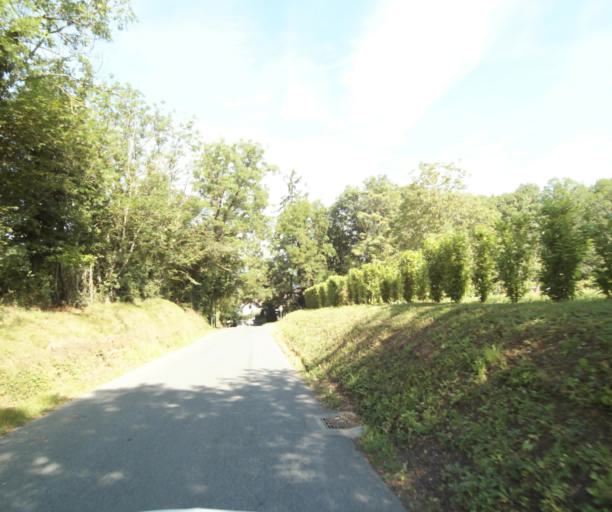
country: FR
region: Rhone-Alpes
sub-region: Departement de la Haute-Savoie
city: Anthy-sur-Leman
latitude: 46.3500
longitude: 6.4069
